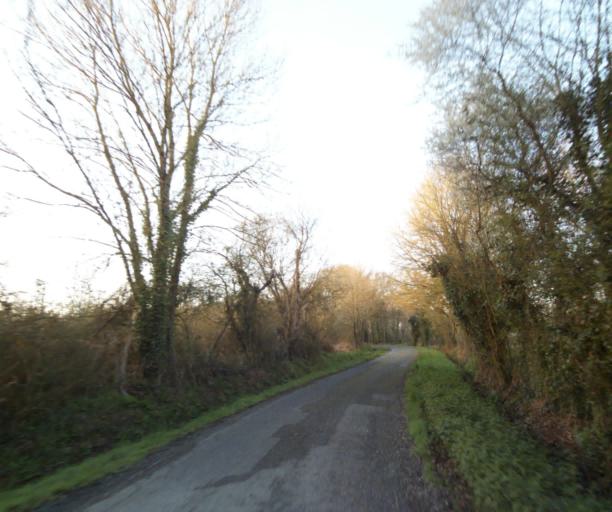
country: FR
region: Pays de la Loire
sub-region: Departement de la Loire-Atlantique
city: Bouvron
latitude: 47.4319
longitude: -1.8853
